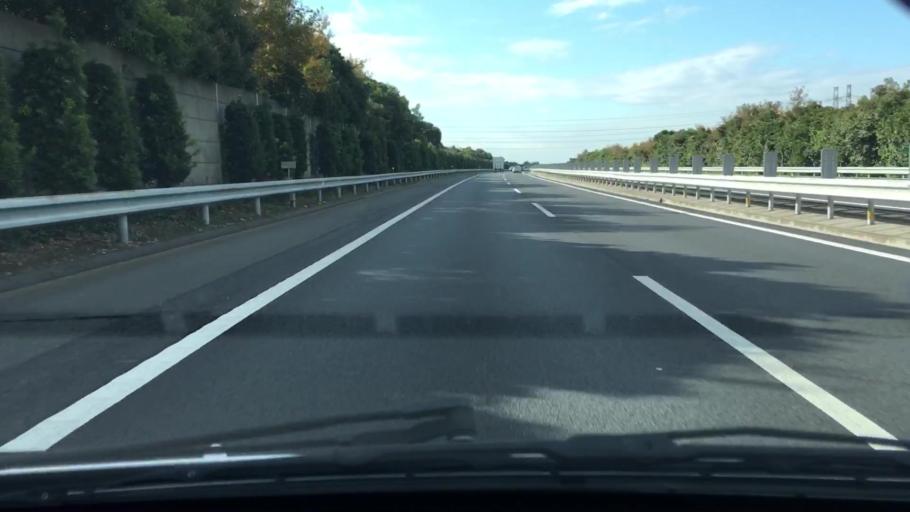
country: JP
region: Chiba
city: Ichihara
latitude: 35.5121
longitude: 140.1139
